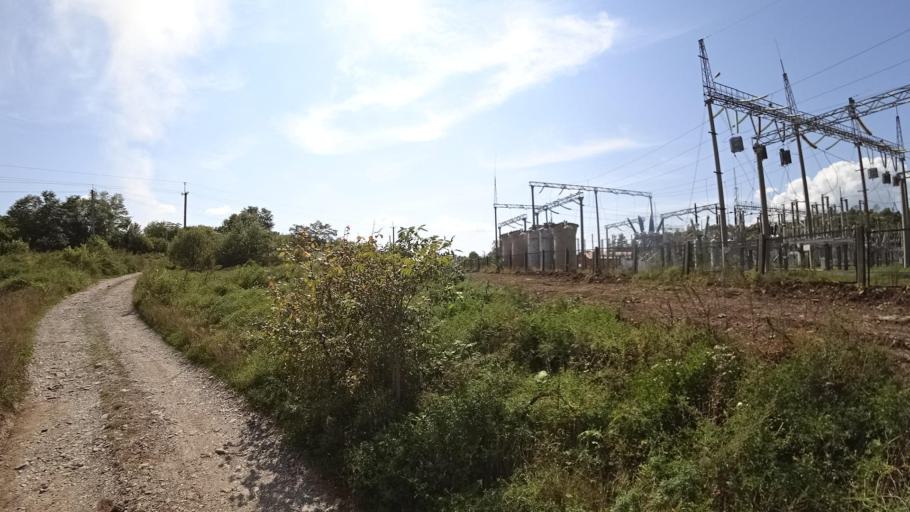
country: RU
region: Jewish Autonomous Oblast
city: Londoko
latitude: 49.0142
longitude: 131.8982
